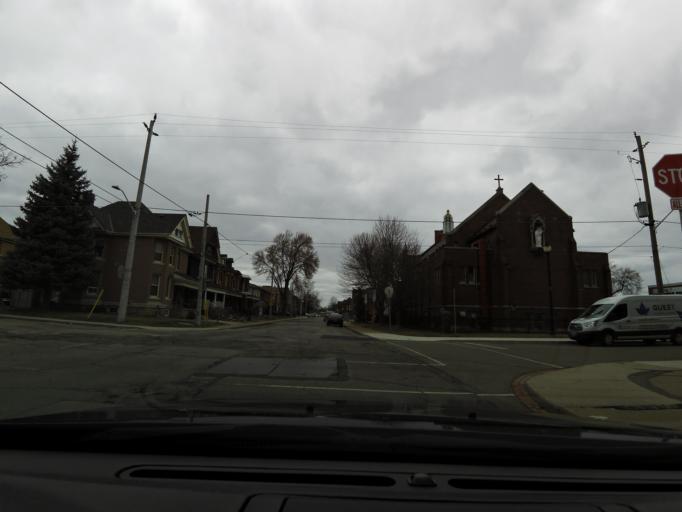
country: CA
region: Ontario
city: Hamilton
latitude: 43.2633
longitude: -79.8695
